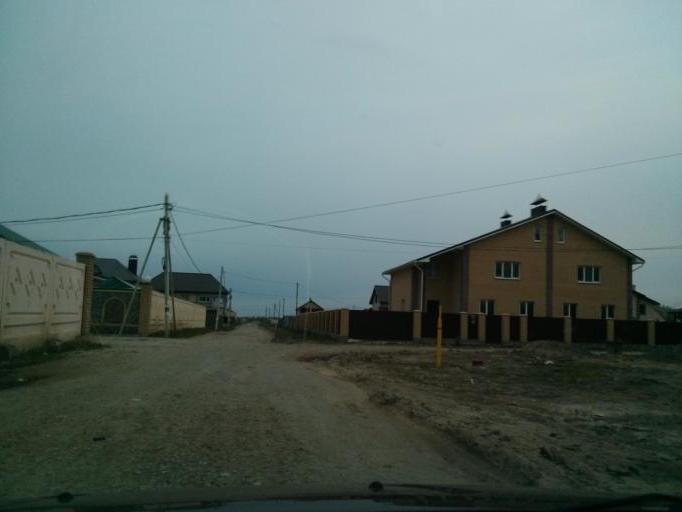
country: RU
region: Vladimir
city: Murom
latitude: 55.5461
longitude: 42.0649
